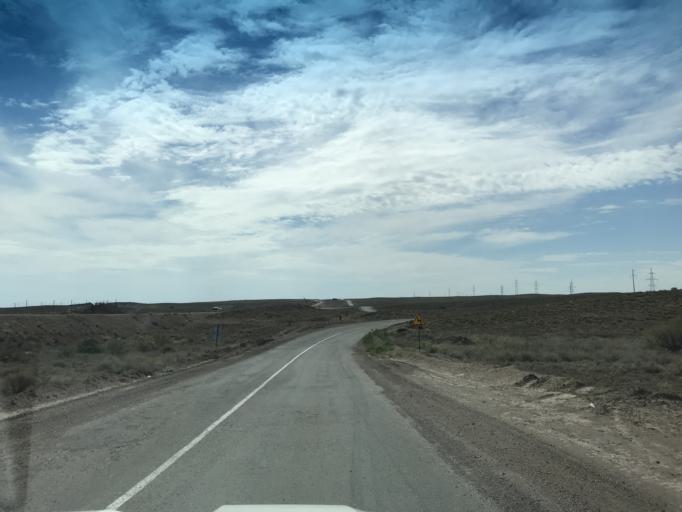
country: KZ
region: Zhambyl
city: Mynaral
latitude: 45.2772
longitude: 73.7810
